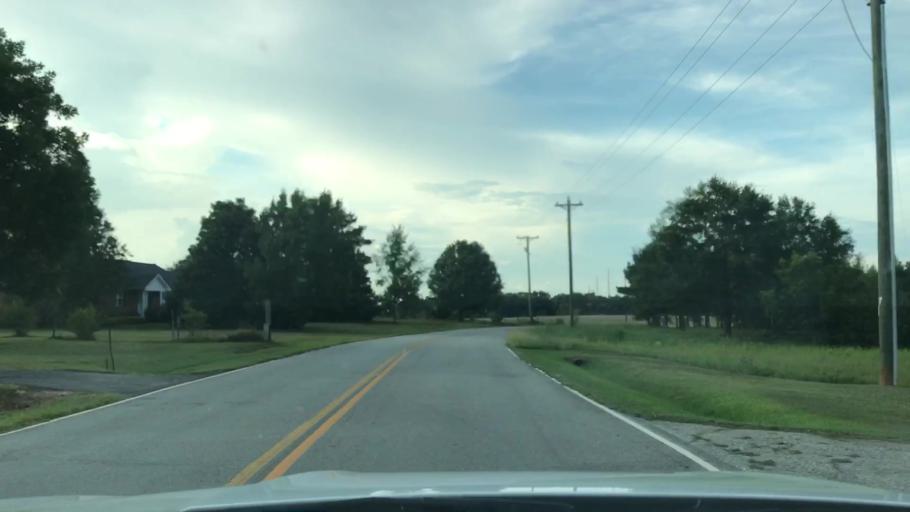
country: US
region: South Carolina
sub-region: Spartanburg County
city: Roebuck
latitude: 34.7868
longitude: -81.9170
